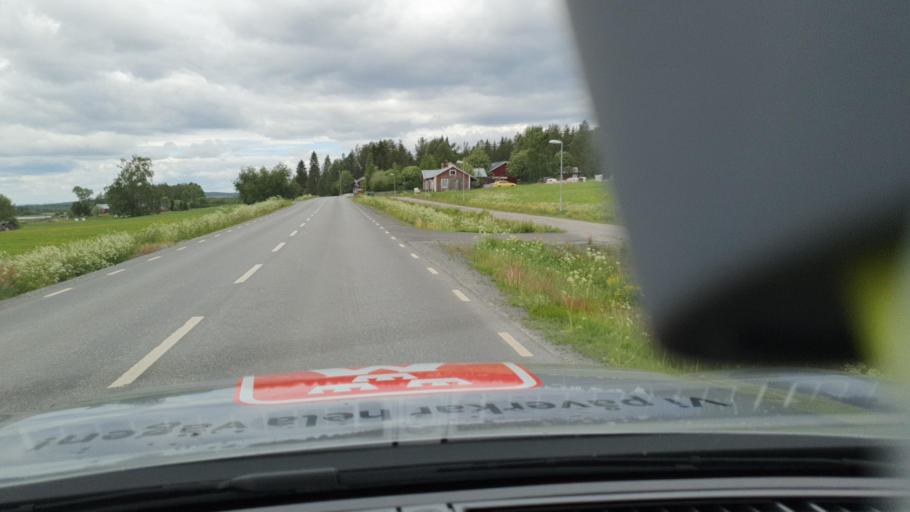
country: SE
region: Norrbotten
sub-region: Lulea Kommun
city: Sodra Sunderbyn
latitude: 65.8130
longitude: 22.0115
